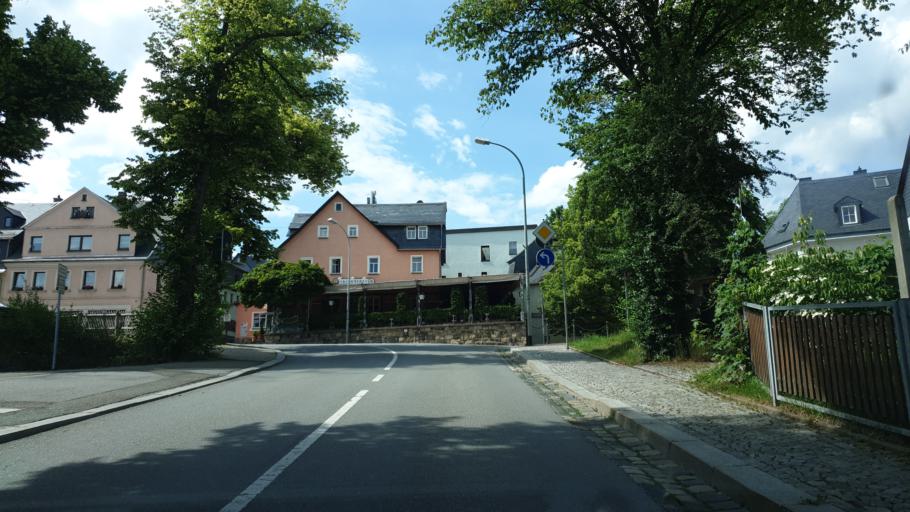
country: DE
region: Saxony
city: Schwarzenberg
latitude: 50.5368
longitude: 12.7822
